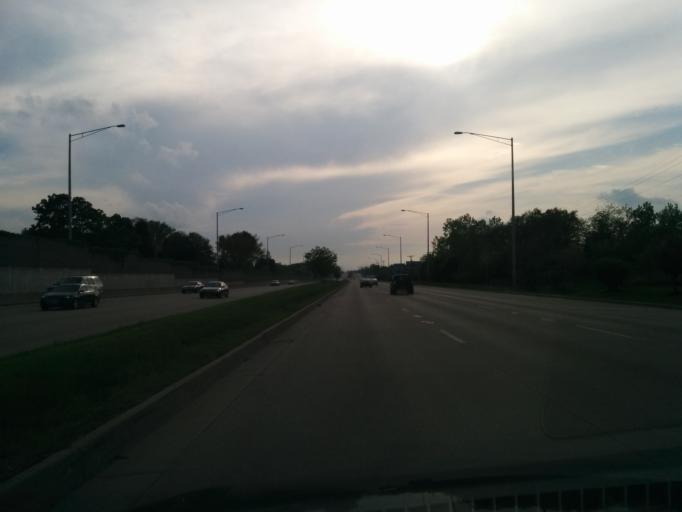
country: US
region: Illinois
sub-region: DuPage County
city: Lombard
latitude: 41.9050
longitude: -88.0095
